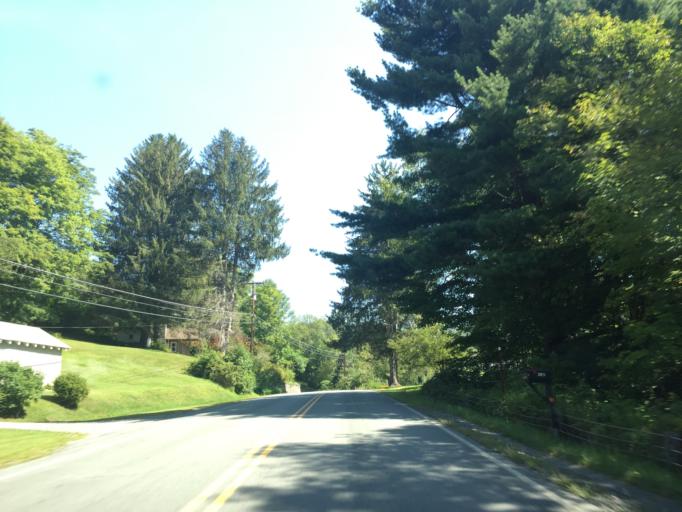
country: US
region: New York
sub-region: Sullivan County
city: Livingston Manor
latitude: 41.8113
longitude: -74.9627
